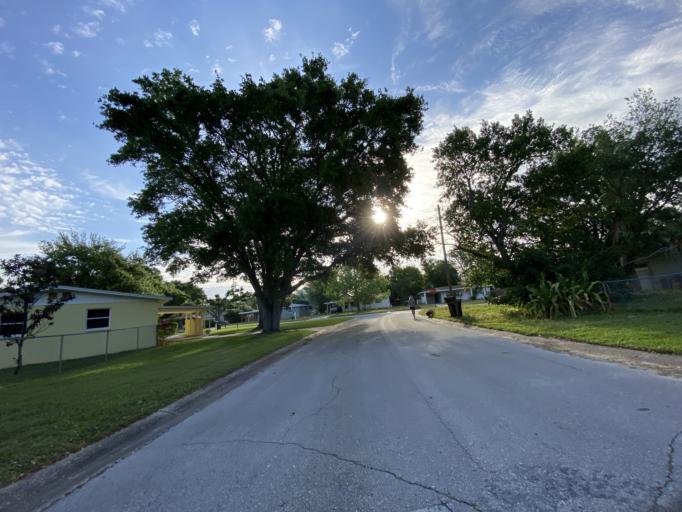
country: US
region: Florida
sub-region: Volusia County
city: South Daytona
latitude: 29.1761
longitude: -81.0133
